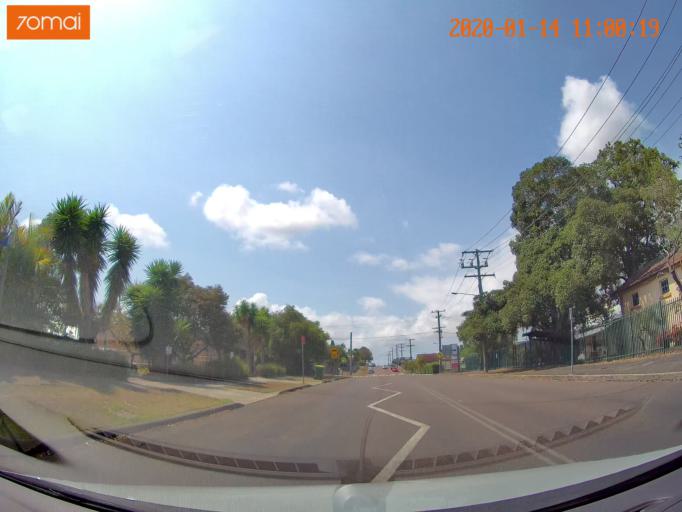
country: AU
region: New South Wales
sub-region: Lake Macquarie Shire
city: Dora Creek
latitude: -33.1052
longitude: 151.4885
